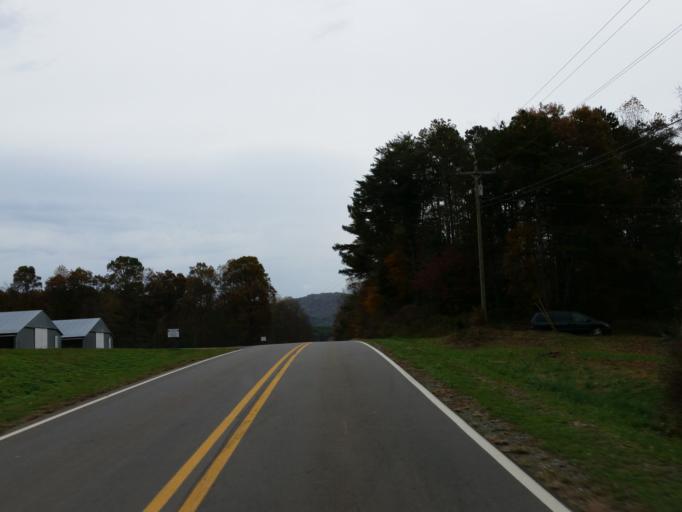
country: US
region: Georgia
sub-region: Gilmer County
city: Ellijay
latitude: 34.6480
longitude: -84.3187
